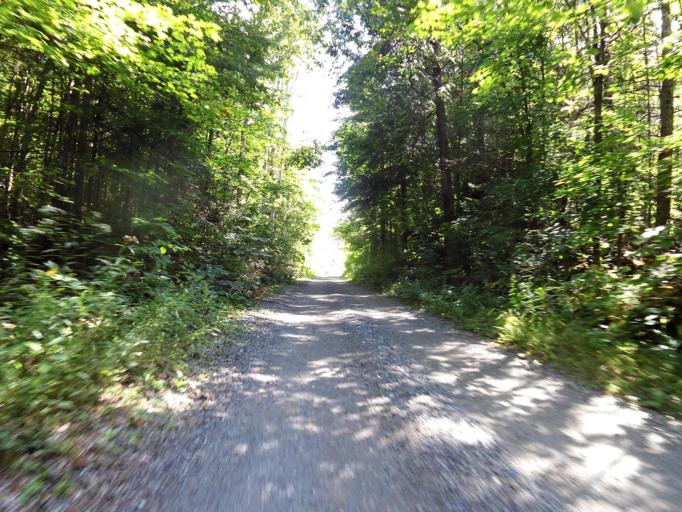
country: CA
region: Ontario
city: Renfrew
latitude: 45.0281
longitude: -76.7050
